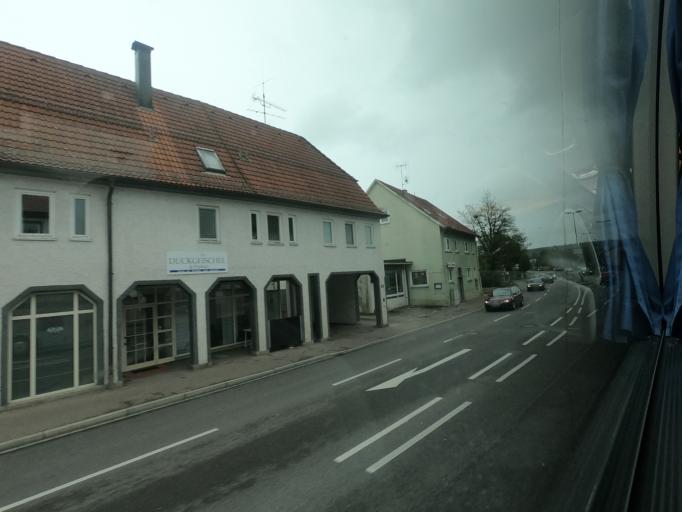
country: DE
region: Baden-Wuerttemberg
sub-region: Regierungsbezirk Stuttgart
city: Heidenheim an der Brenz
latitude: 48.7073
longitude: 10.1626
